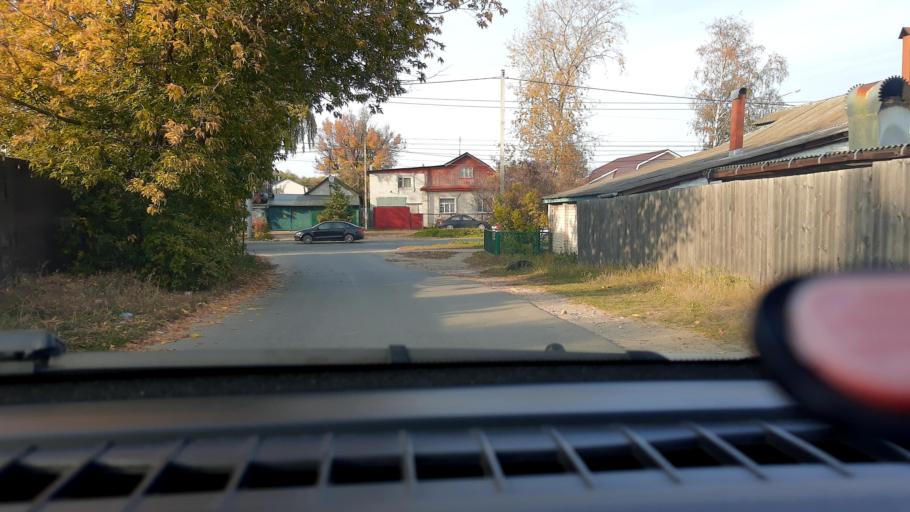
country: RU
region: Nizjnij Novgorod
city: Lukino
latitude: 56.3887
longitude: 43.7480
